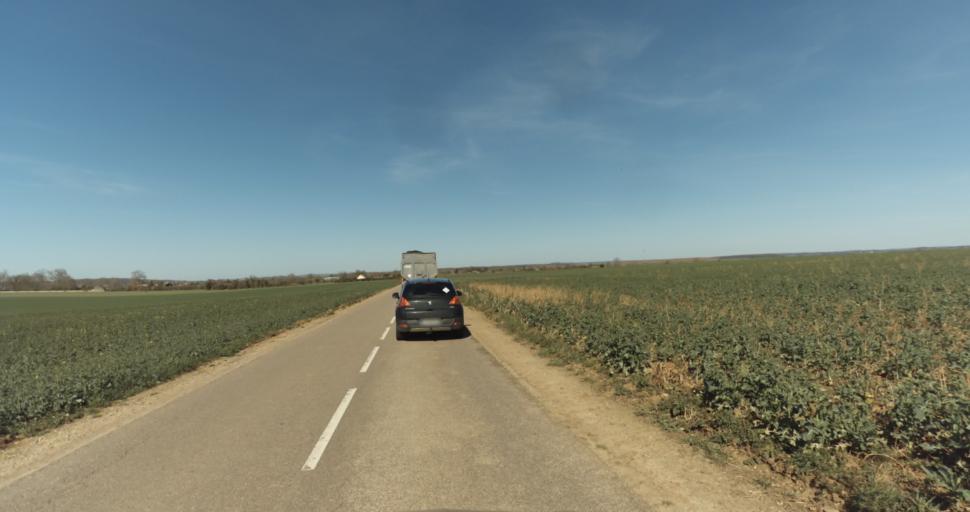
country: FR
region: Lower Normandy
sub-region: Departement du Calvados
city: Canon
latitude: 49.0443
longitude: -0.0677
